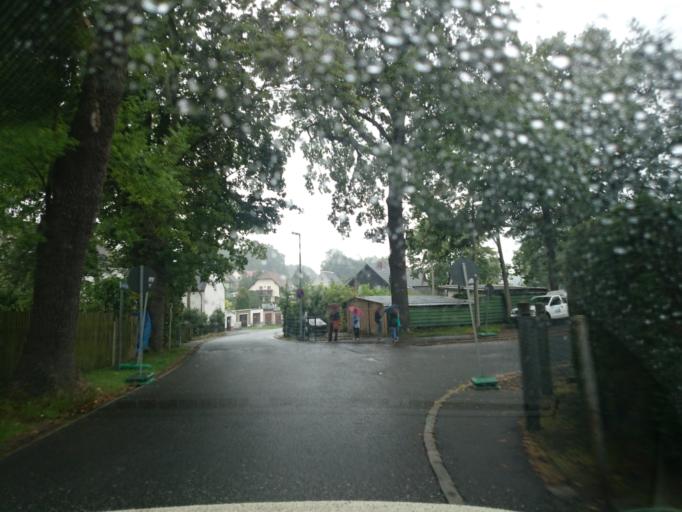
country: DE
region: Saxony
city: Brand-Erbisdorf
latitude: 50.8640
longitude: 13.3156
